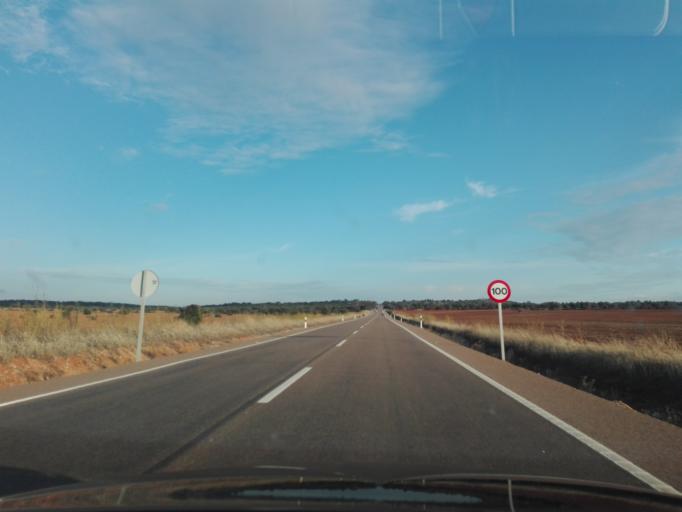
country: ES
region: Extremadura
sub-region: Provincia de Badajoz
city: Usagre
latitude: 38.3719
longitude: -6.2510
